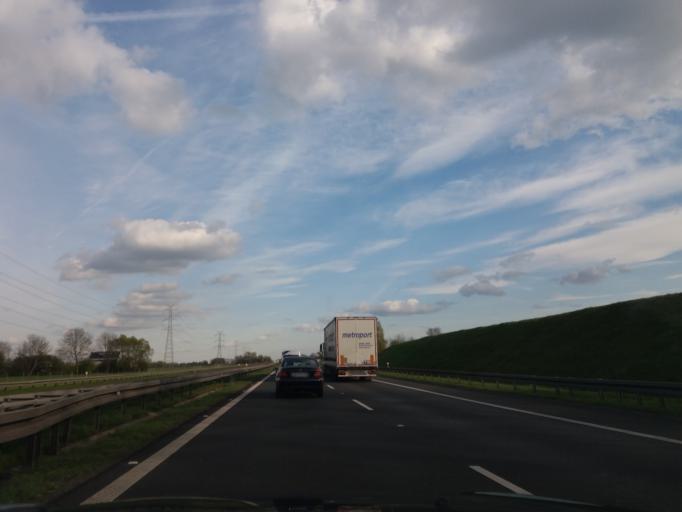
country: PL
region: Lower Silesian Voivodeship
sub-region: Powiat olawski
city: Wierzbno
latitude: 50.9275
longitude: 17.1237
